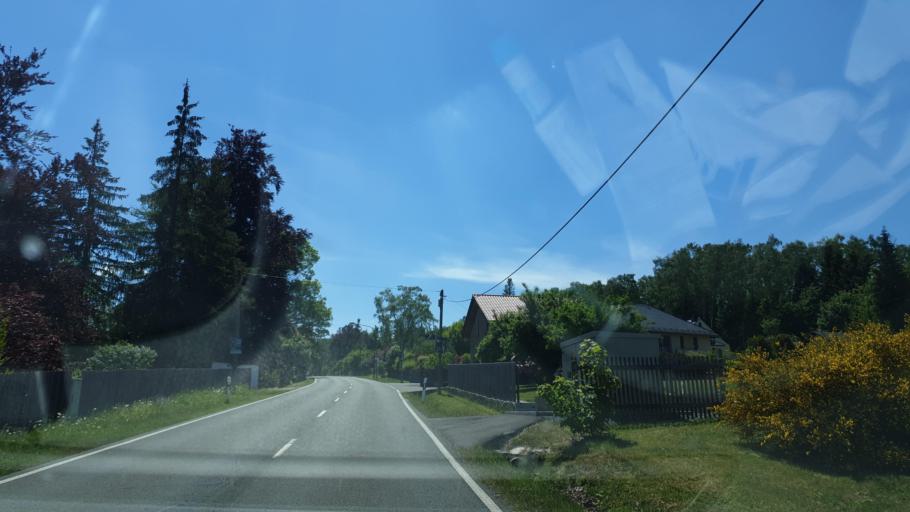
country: DE
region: Saxony
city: Falkenstein
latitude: 50.4650
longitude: 12.3662
